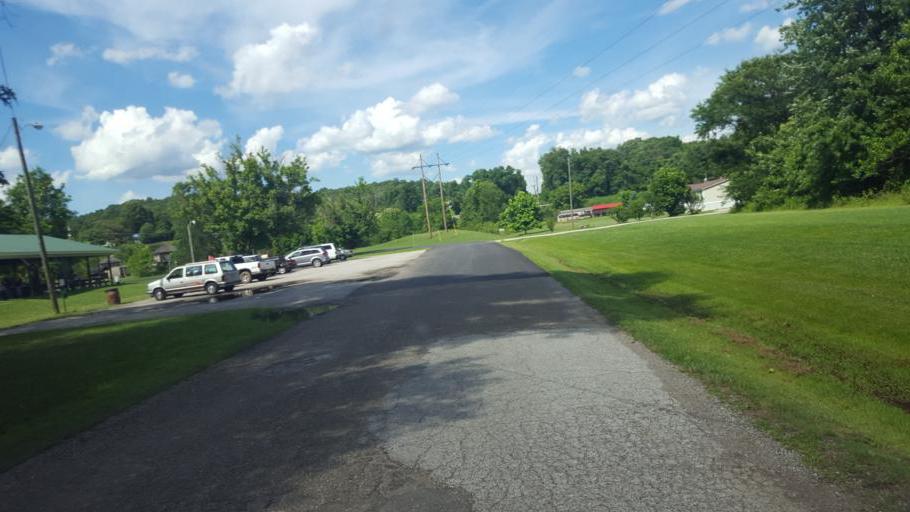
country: US
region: West Virginia
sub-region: Mason County
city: Point Pleasant
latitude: 38.8358
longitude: -82.1229
